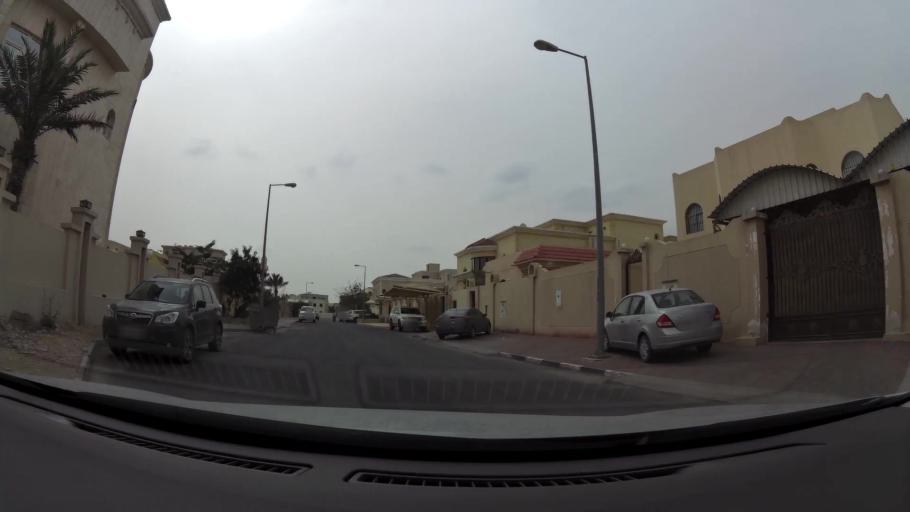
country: QA
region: Baladiyat ad Dawhah
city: Doha
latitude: 25.2484
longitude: 51.5226
